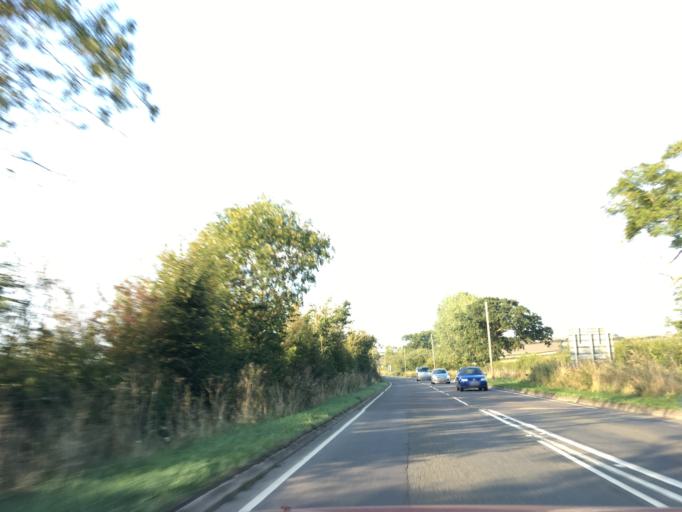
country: GB
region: England
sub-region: Warwickshire
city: Shipston on Stour
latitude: 52.0577
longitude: -1.6601
